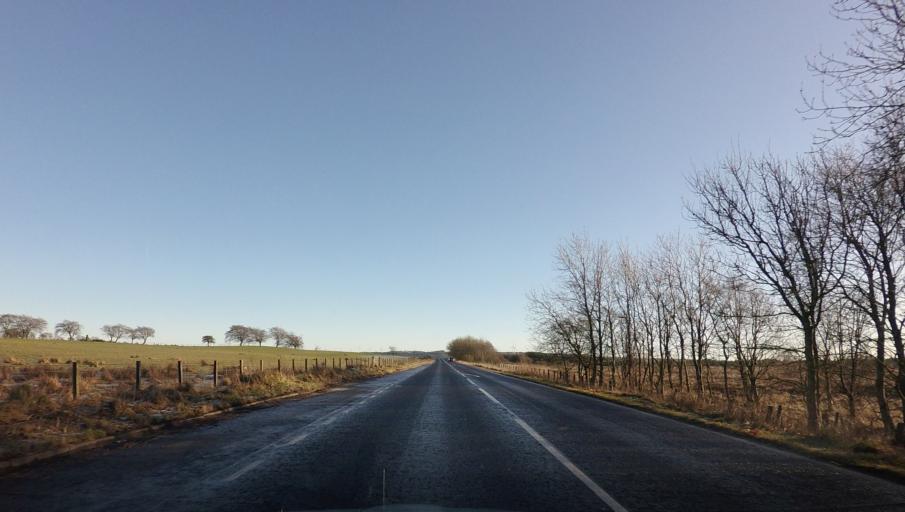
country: GB
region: Scotland
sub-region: North Lanarkshire
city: Shotts
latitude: 55.8055
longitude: -3.7706
